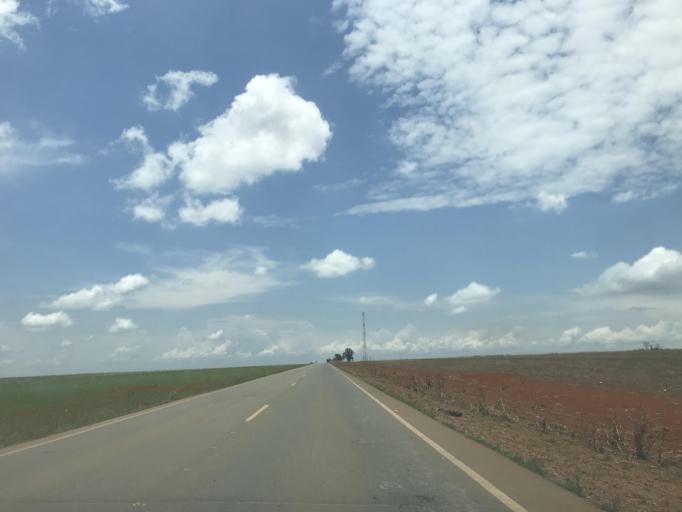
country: BR
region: Goias
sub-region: Vianopolis
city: Vianopolis
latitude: -16.5309
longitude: -48.2459
